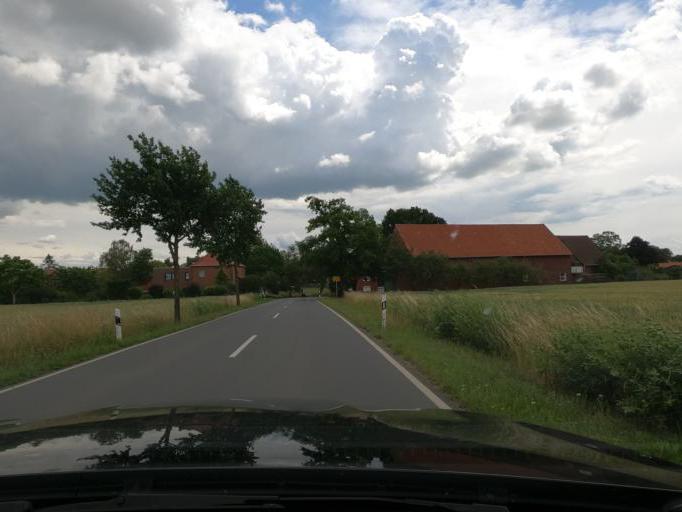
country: DE
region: Lower Saxony
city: Sehnde
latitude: 52.2878
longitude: 10.0128
